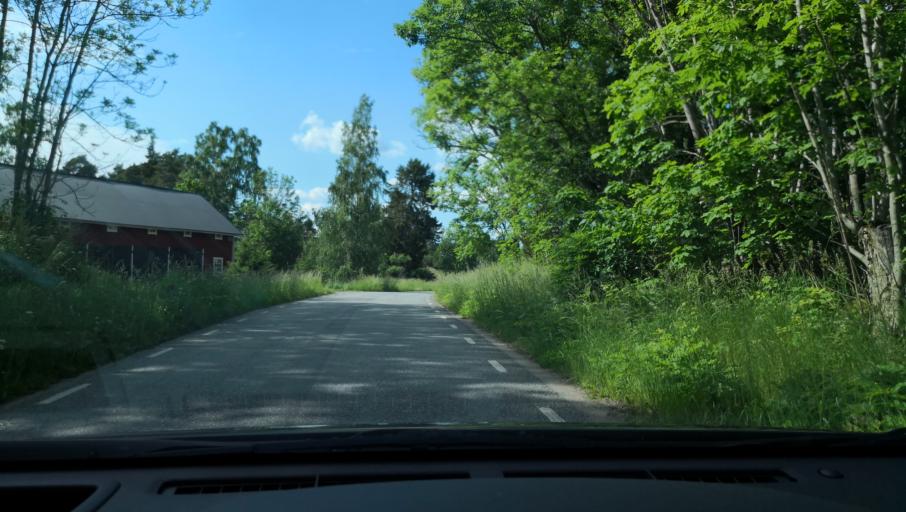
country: SE
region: Uppsala
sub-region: Enkopings Kommun
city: Orsundsbro
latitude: 59.8251
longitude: 17.3203
